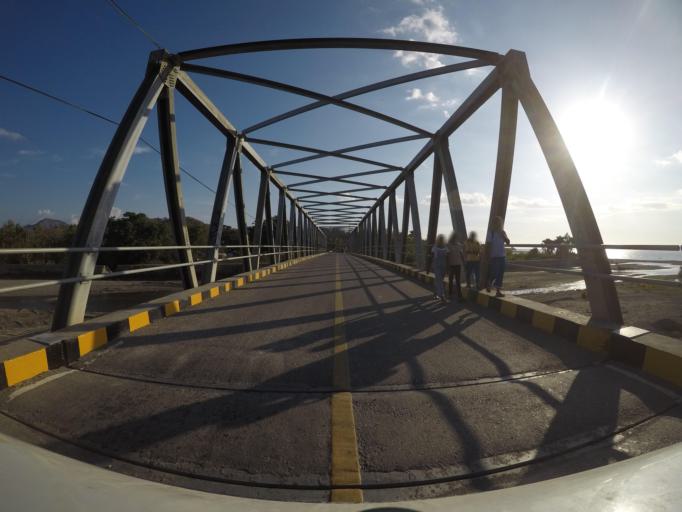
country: ID
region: East Nusa Tenggara
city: Atambua
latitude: -8.9456
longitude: 124.9747
